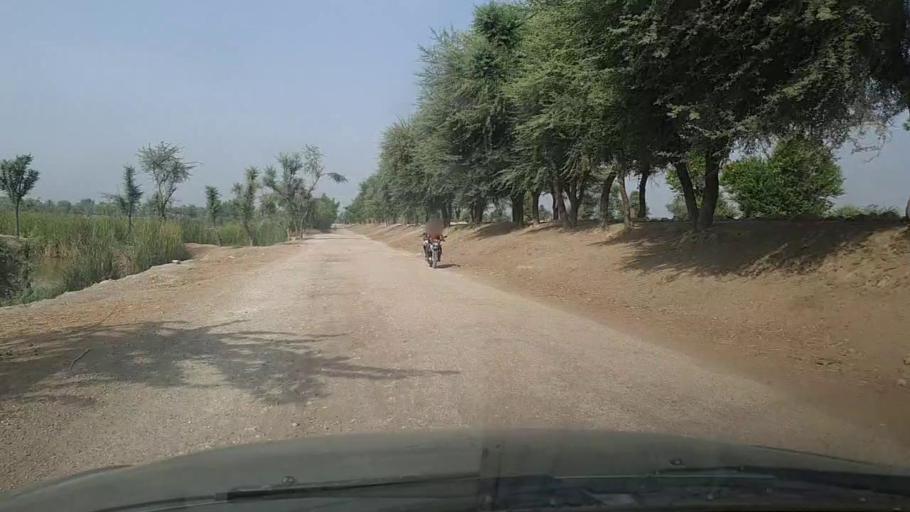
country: PK
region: Sindh
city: Pir jo Goth
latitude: 27.5250
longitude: 68.4912
